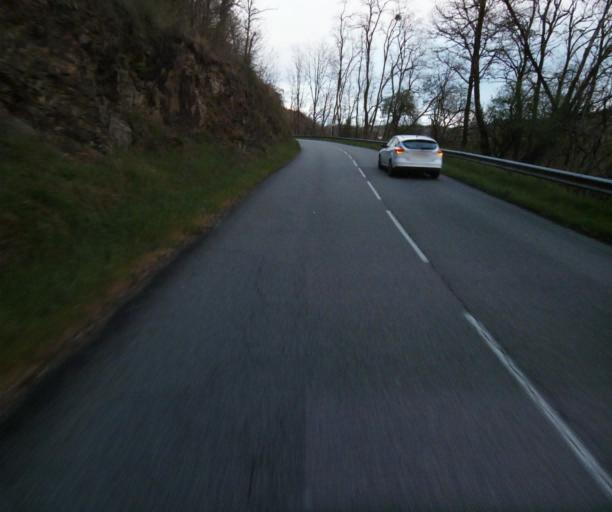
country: FR
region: Limousin
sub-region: Departement de la Correze
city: Laguenne
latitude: 45.2514
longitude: 1.7894
